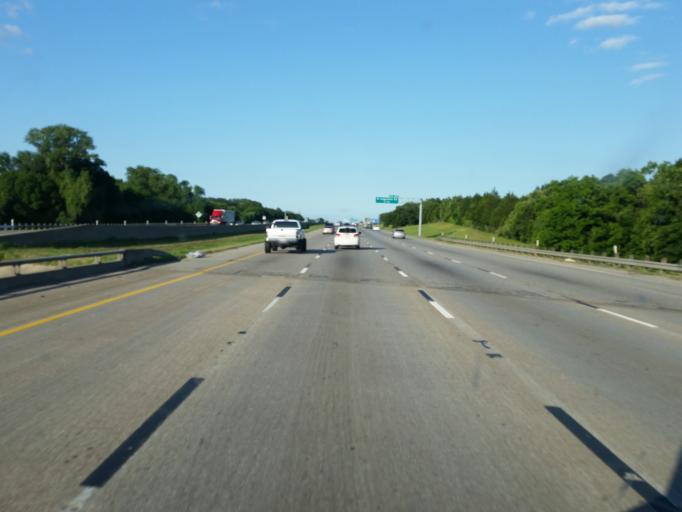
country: US
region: Texas
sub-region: Dallas County
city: Hutchins
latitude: 32.6798
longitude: -96.6710
